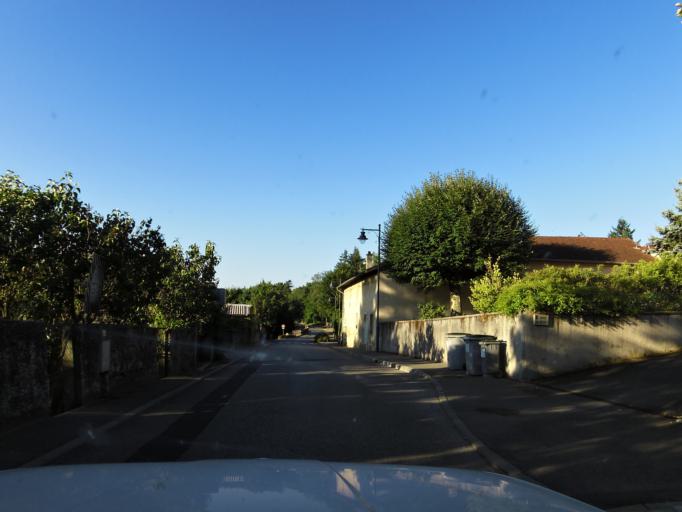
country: FR
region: Rhone-Alpes
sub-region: Departement de l'Ain
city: Saint-Jean-de-Niost
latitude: 45.8683
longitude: 5.2240
